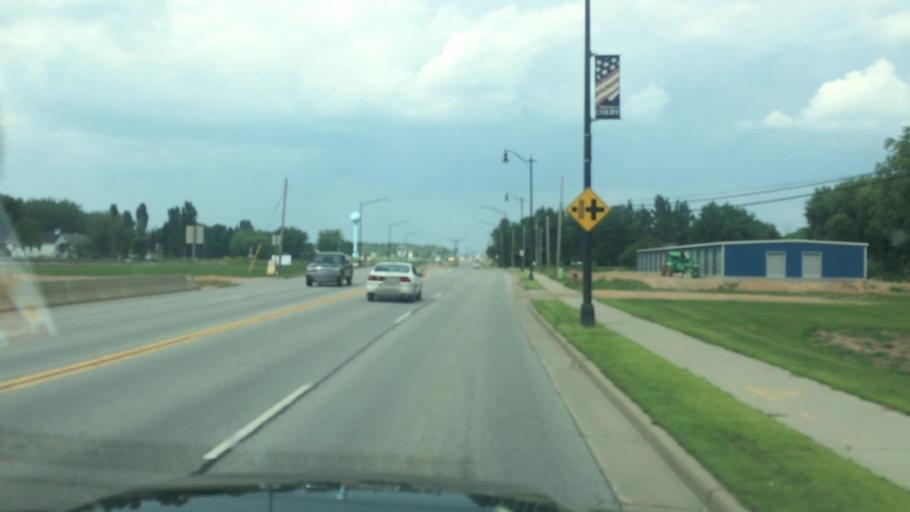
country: US
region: Wisconsin
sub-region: Clark County
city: Colby
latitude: 44.9119
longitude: -90.3154
